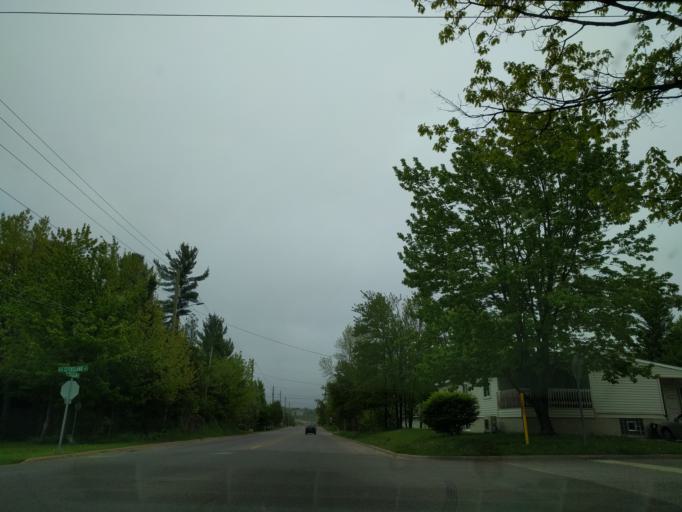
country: US
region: Michigan
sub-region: Marquette County
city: Trowbridge Park
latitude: 46.5519
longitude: -87.4199
